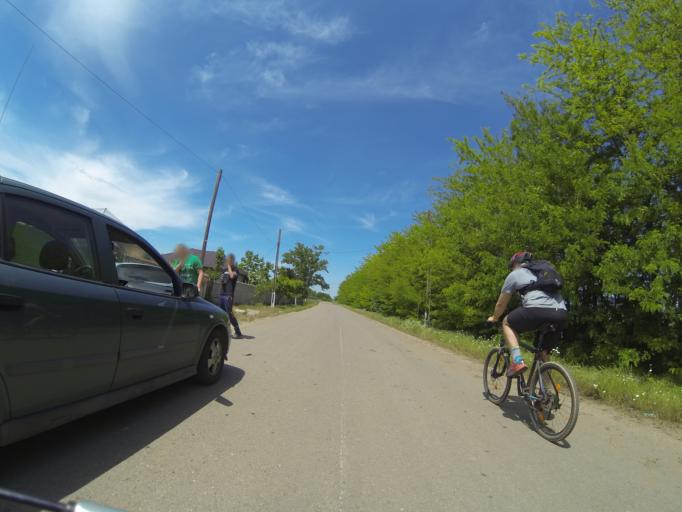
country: RO
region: Dolj
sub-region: Comuna Diosti
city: Radomir
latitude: 44.1606
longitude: 24.1623
